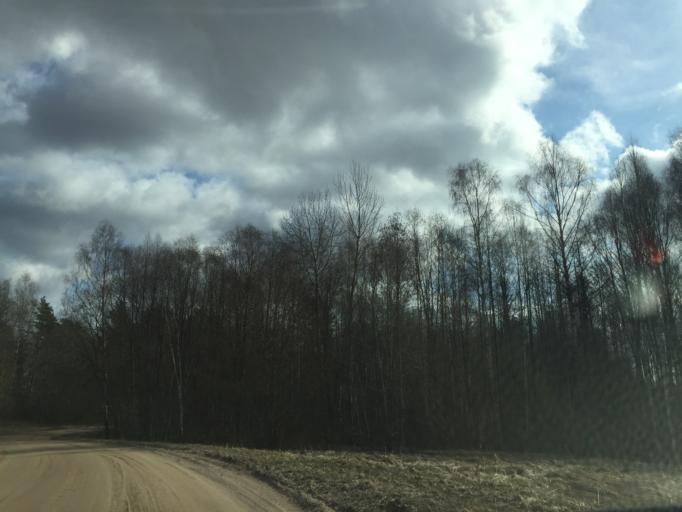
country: LV
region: Vecumnieki
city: Vecumnieki
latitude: 56.5839
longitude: 24.5833
